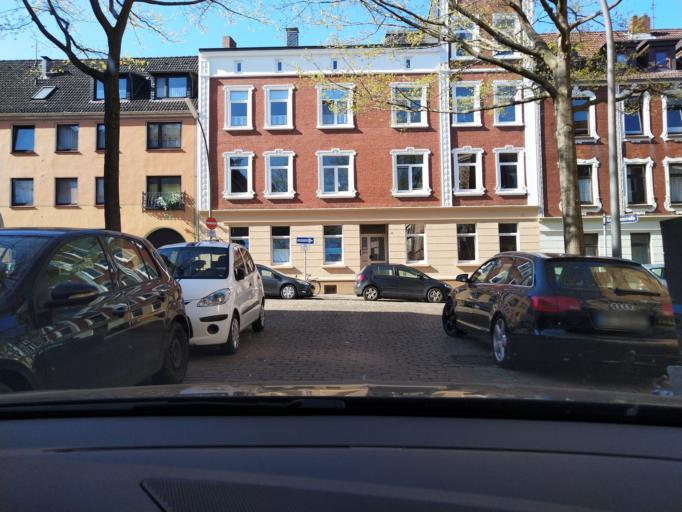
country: DE
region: Hamburg
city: Harburg
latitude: 53.4578
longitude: 9.9739
